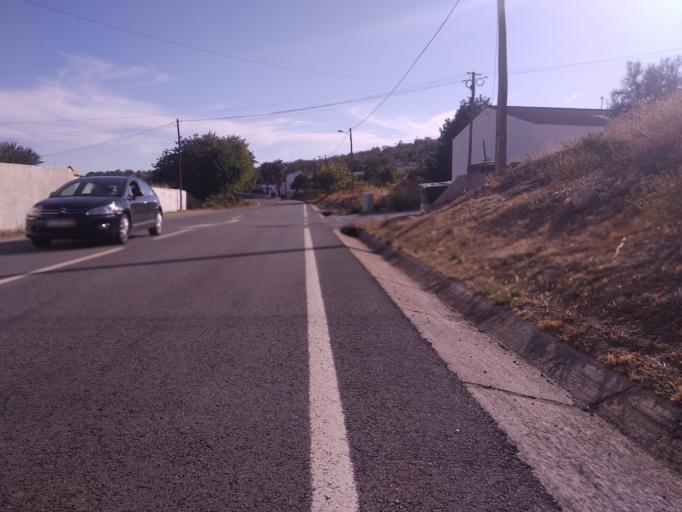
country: PT
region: Faro
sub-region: Sao Bras de Alportel
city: Sao Bras de Alportel
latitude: 37.1143
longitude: -7.9078
